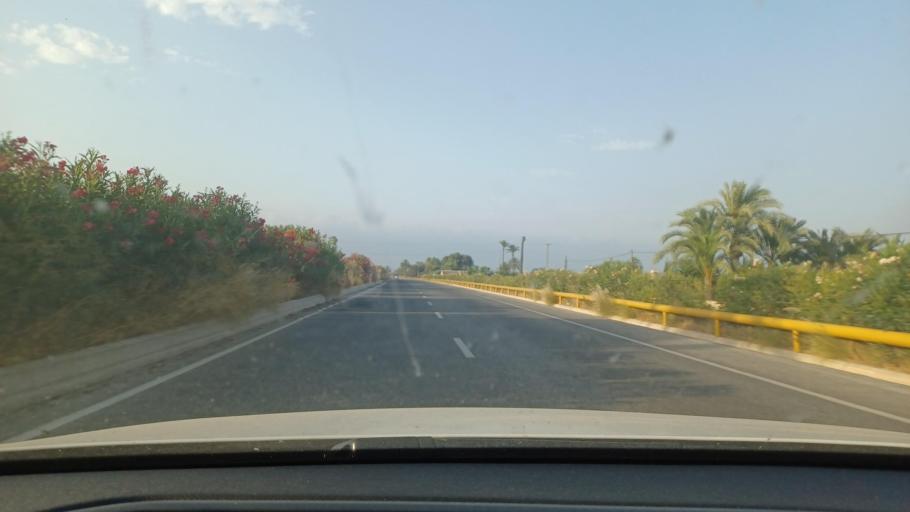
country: ES
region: Valencia
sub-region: Provincia de Alicante
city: Elche
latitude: 38.2024
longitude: -0.7003
